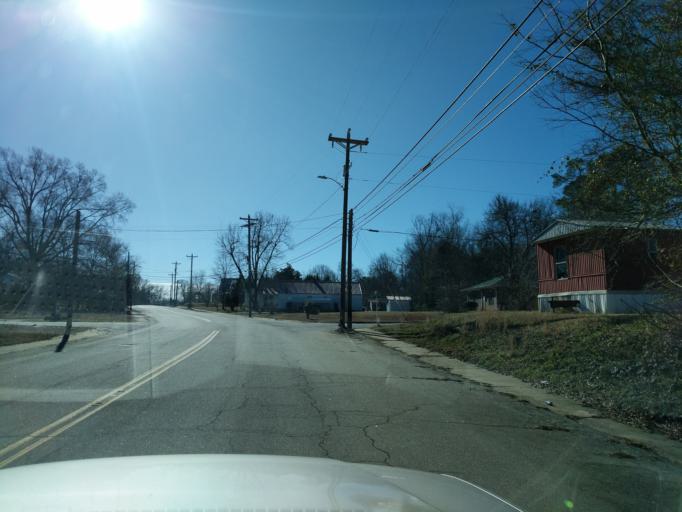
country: US
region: South Carolina
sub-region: Laurens County
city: Clinton
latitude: 34.4835
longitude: -81.8818
